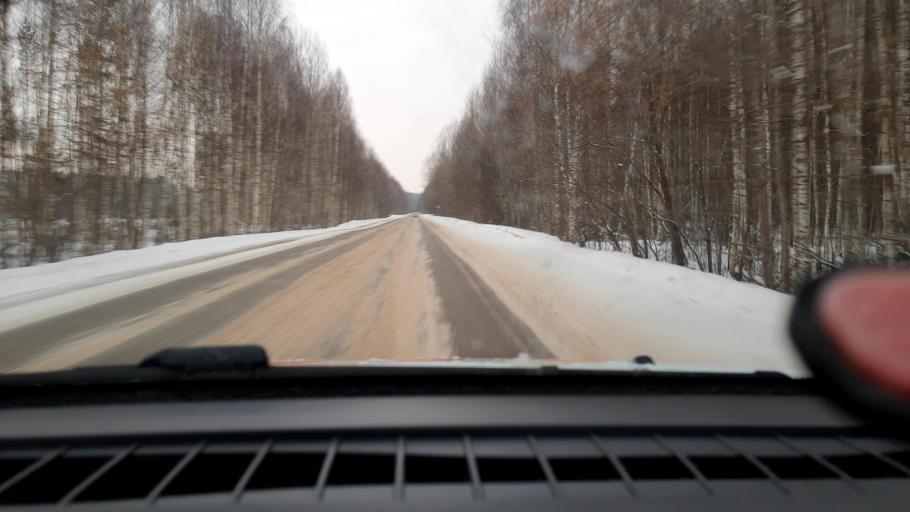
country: RU
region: Nizjnij Novgorod
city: Pamyat' Parizhskoy Kommuny
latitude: 56.2745
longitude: 44.4023
